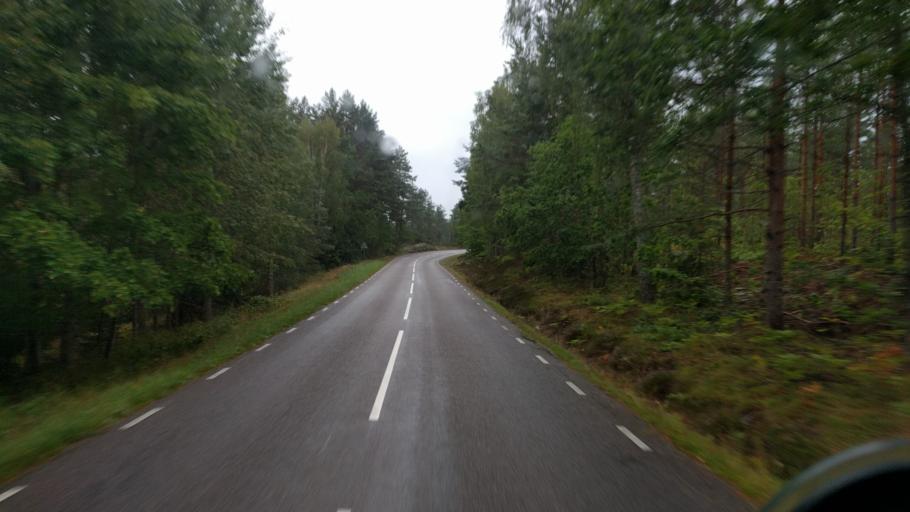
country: SE
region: Kalmar
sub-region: Vasterviks Kommun
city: Gamleby
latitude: 57.8035
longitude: 16.4164
